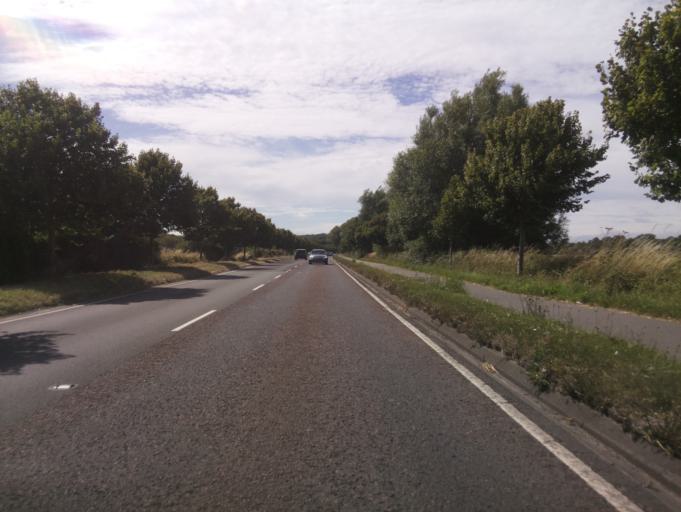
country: GB
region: England
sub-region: Dorset
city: Dorchester
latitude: 50.7212
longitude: -2.4472
